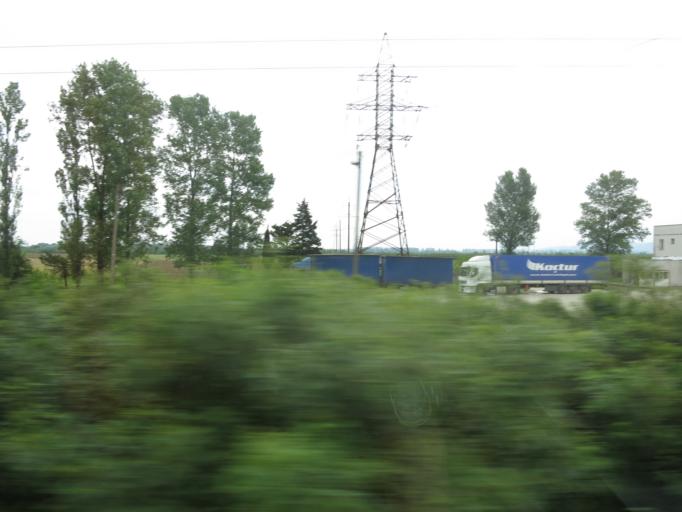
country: GE
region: Imereti
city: Samtredia
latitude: 42.1337
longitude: 42.3352
